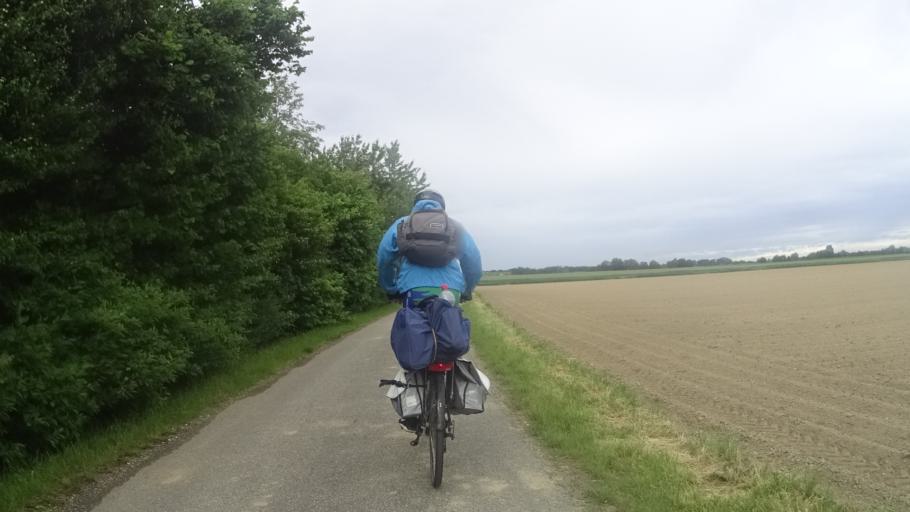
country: DE
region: Bavaria
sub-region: Upper Bavaria
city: Bockhorn
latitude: 48.3114
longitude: 11.9743
